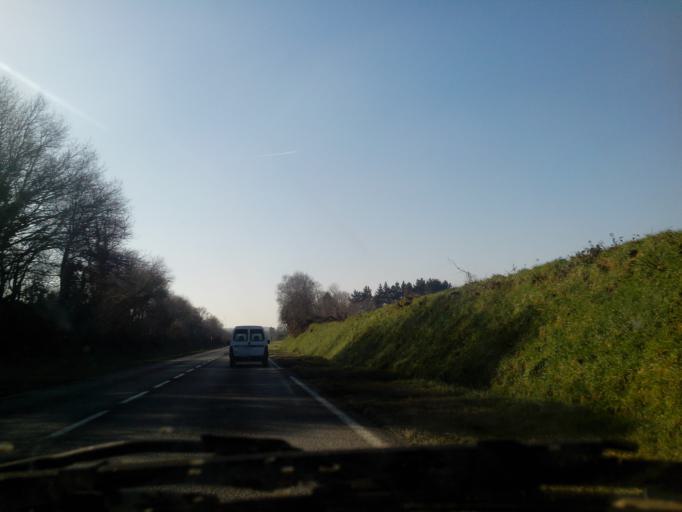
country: FR
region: Brittany
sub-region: Departement des Cotes-d'Armor
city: Plemet
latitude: 48.1752
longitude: -2.5658
